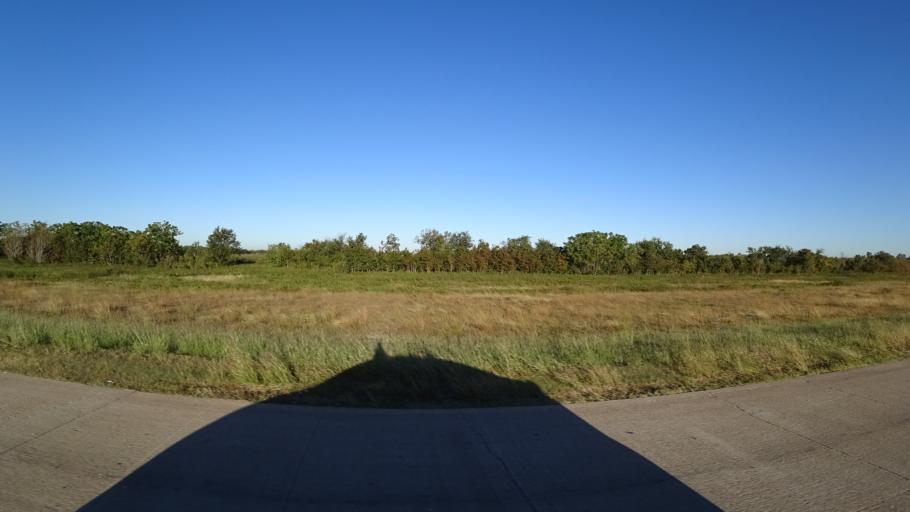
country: US
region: Texas
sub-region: Travis County
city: Hornsby Bend
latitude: 30.2393
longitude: -97.6157
